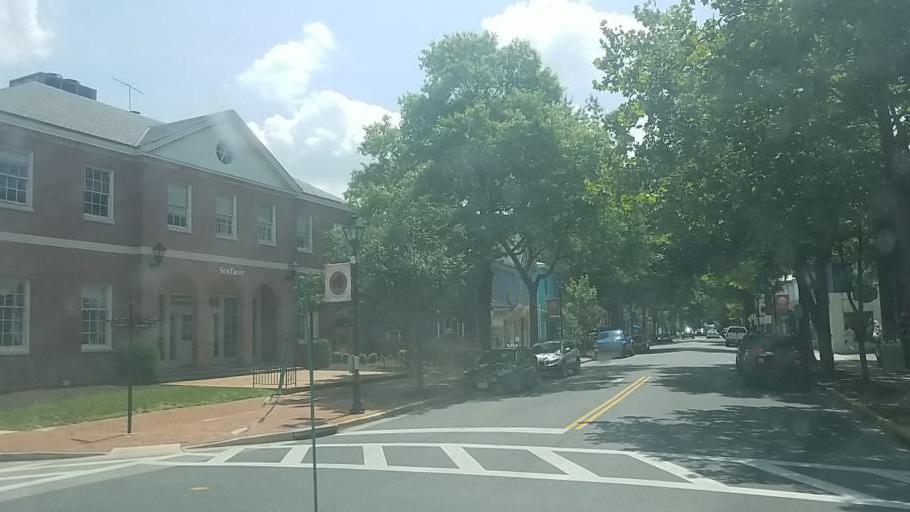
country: US
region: Maryland
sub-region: Talbot County
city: Easton
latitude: 38.7757
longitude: -76.0751
